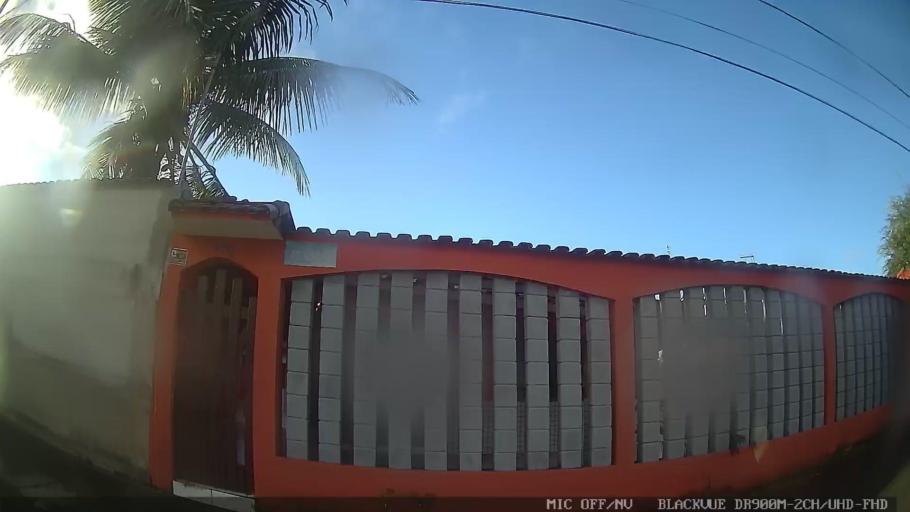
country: BR
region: Sao Paulo
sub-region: Itanhaem
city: Itanhaem
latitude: -24.2351
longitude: -46.8828
